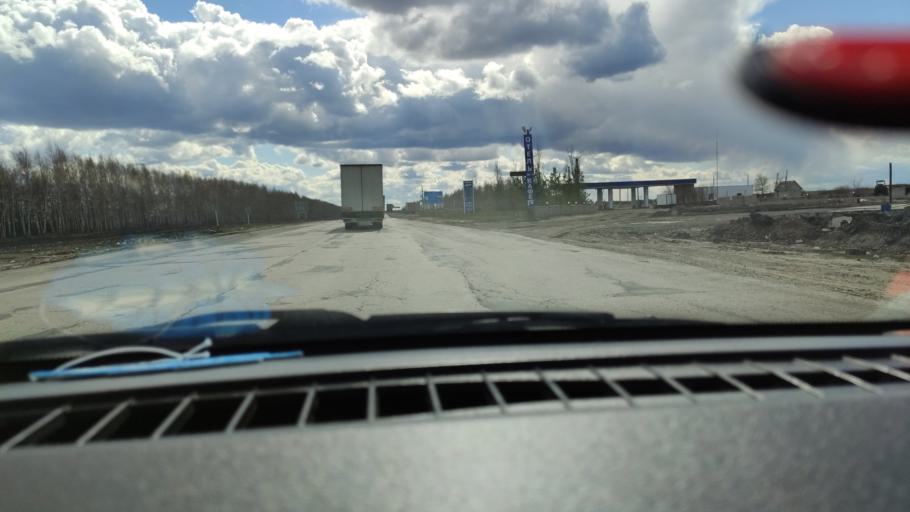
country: RU
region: Samara
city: Syzran'
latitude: 52.9941
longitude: 48.3243
